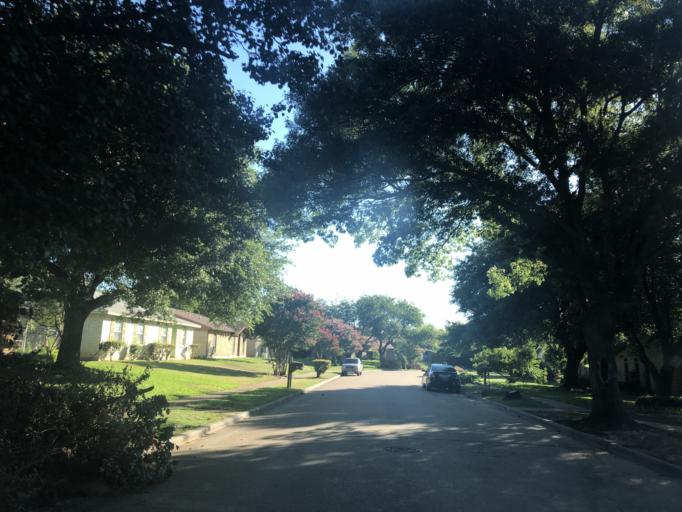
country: US
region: Texas
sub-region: Dallas County
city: Duncanville
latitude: 32.6376
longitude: -96.9479
